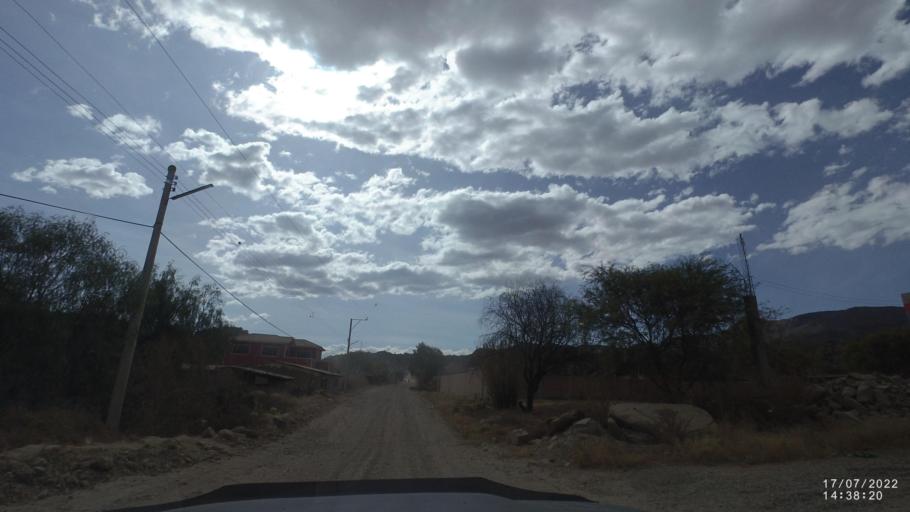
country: BO
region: Cochabamba
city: Capinota
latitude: -17.6445
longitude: -66.2469
